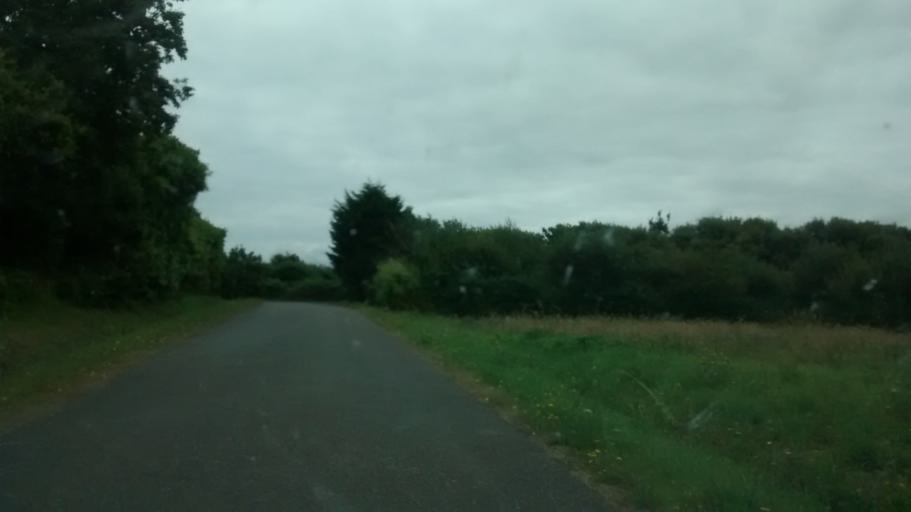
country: FR
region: Brittany
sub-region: Departement du Finistere
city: Lanveoc
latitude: 48.3319
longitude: -4.4375
